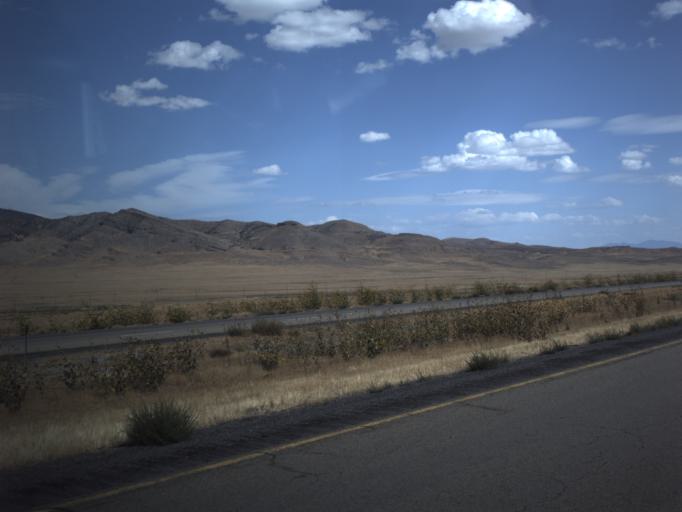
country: US
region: Utah
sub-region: Tooele County
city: Grantsville
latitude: 40.8203
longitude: -112.8869
